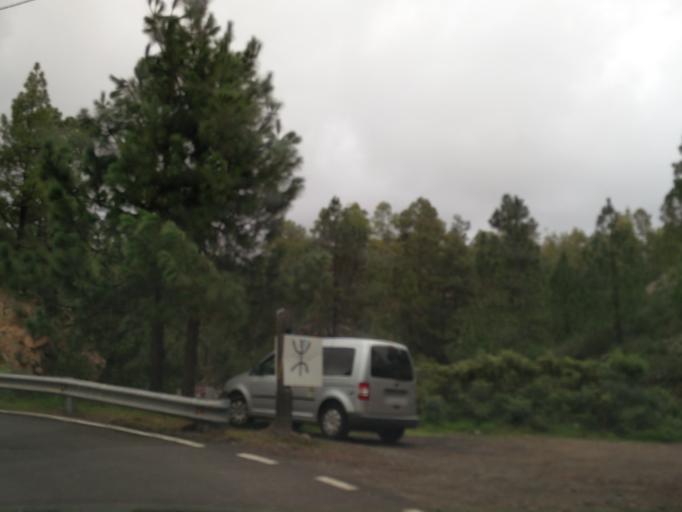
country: ES
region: Canary Islands
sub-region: Provincia de Santa Cruz de Tenerife
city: Arona
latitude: 28.1355
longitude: -16.6874
